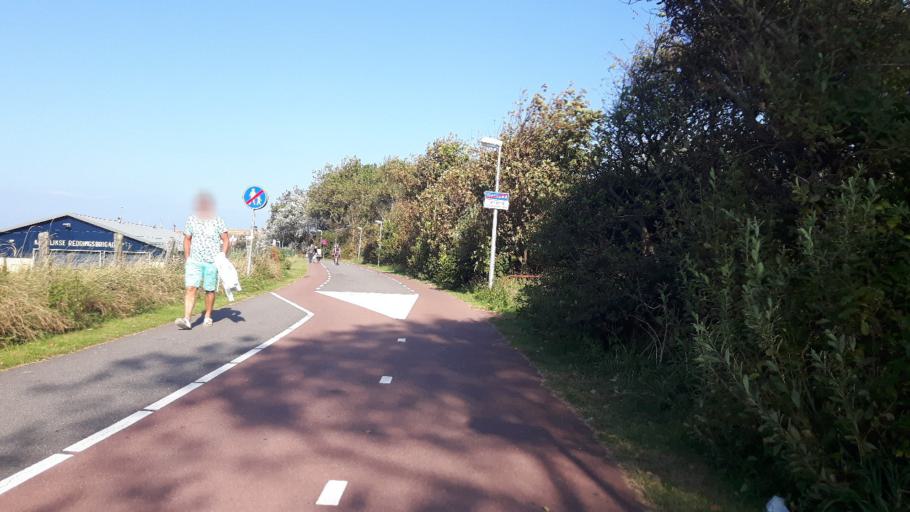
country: NL
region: South Holland
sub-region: Gemeente Katwijk
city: Katwijk aan Zee
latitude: 52.2076
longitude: 4.4088
